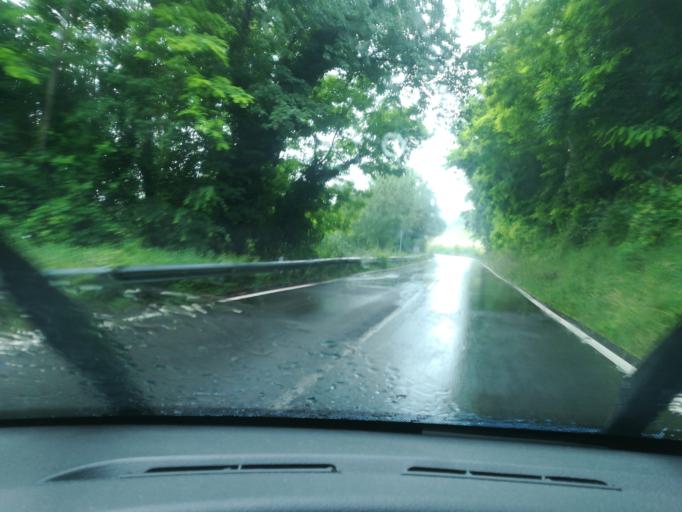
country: IT
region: The Marches
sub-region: Provincia di Macerata
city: Sarnano
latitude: 43.0109
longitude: 13.3271
